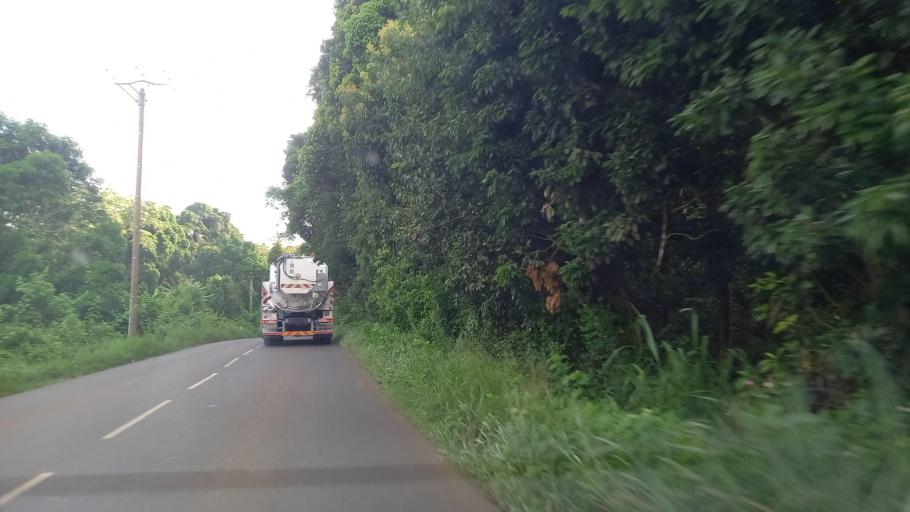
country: YT
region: Chiconi
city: Chiconi
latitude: -12.8100
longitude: 45.1276
